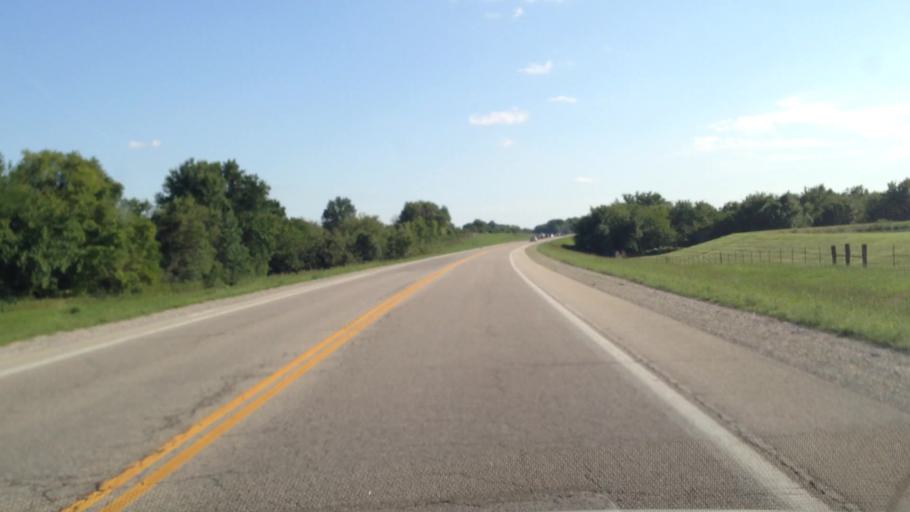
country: US
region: Kansas
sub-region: Crawford County
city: Arma
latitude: 37.5378
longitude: -94.7093
